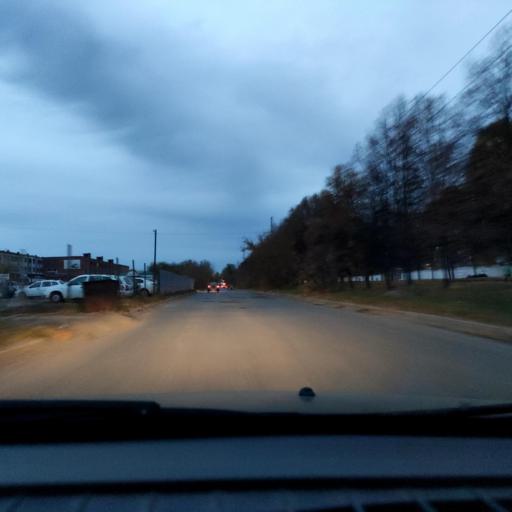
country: RU
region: Samara
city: Tol'yatti
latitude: 53.5384
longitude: 49.3072
